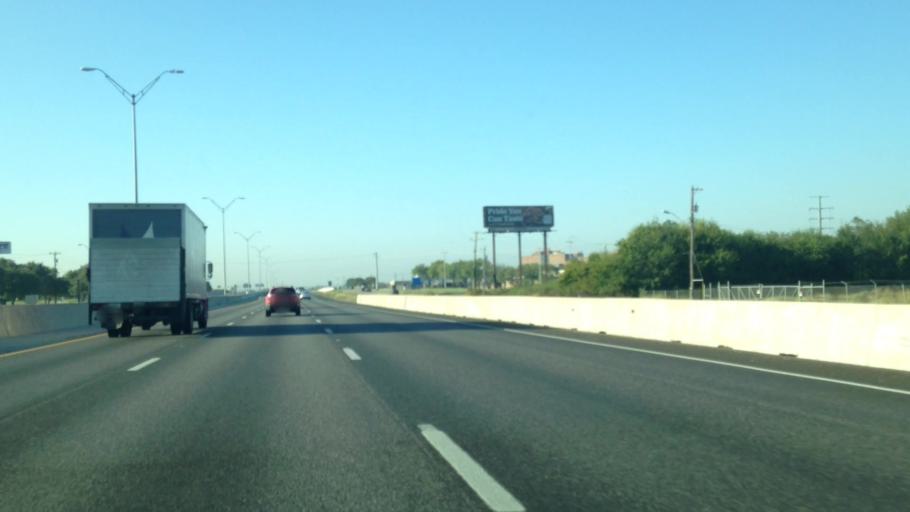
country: US
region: Texas
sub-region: Bexar County
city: Kirby
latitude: 29.4680
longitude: -98.4074
